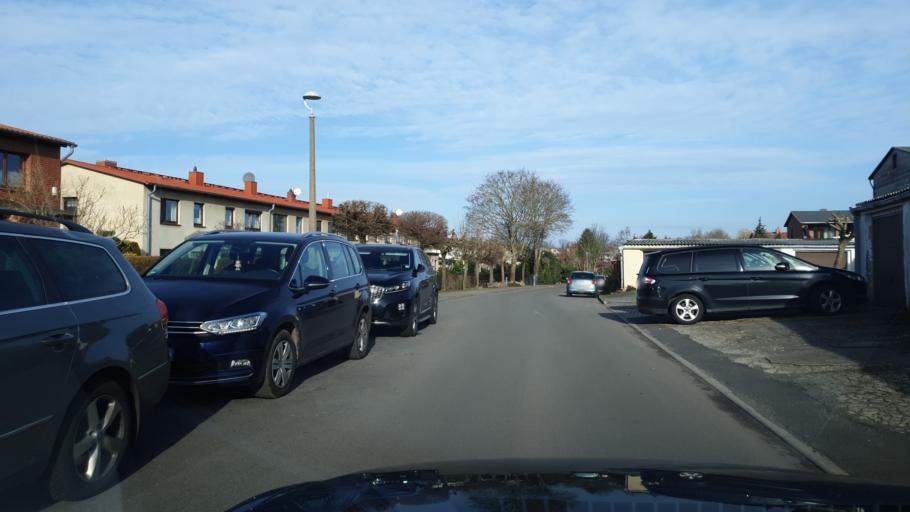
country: DE
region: Mecklenburg-Vorpommern
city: Lankow
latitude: 53.6435
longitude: 11.3589
